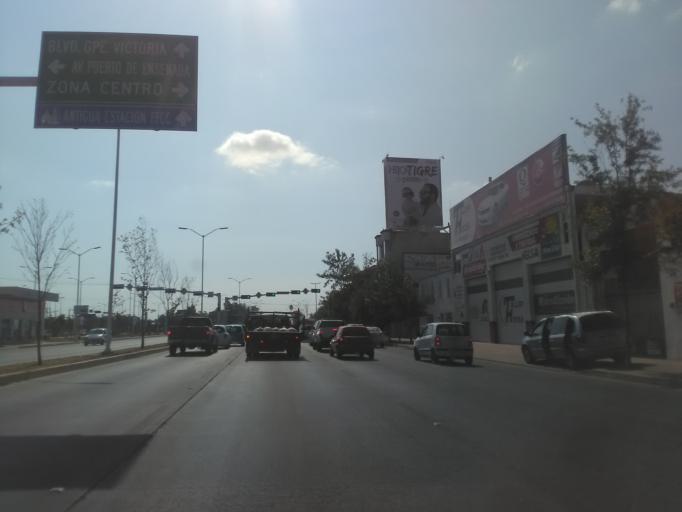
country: MX
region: Durango
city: Victoria de Durango
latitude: 24.0361
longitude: -104.6776
